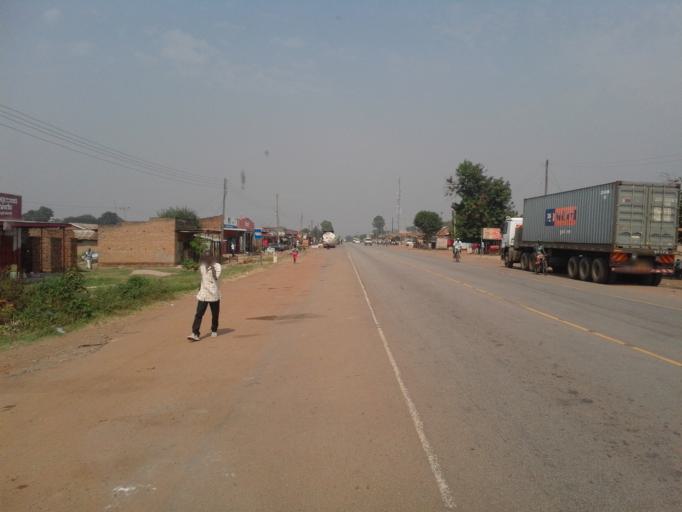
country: UG
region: Eastern Region
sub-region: Bugiri District
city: Bugiri
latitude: 0.6032
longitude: 33.6941
